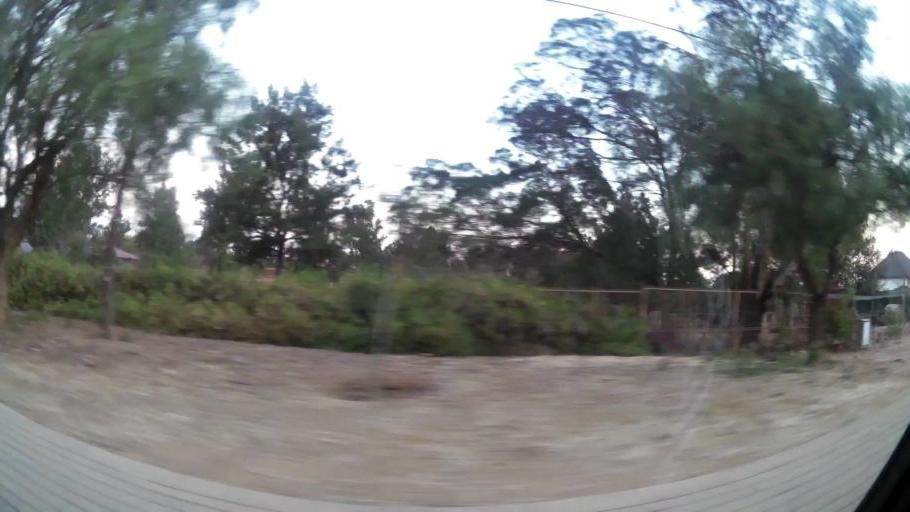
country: ZA
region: Gauteng
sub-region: City of Johannesburg Metropolitan Municipality
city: Midrand
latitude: -25.9746
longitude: 28.0750
